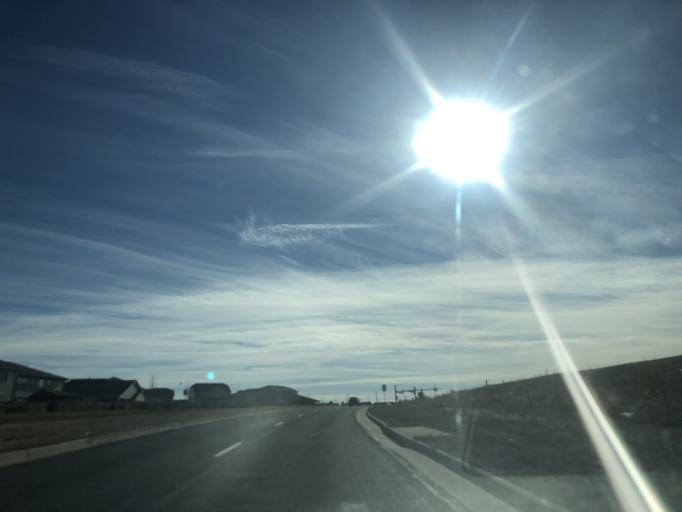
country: US
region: Colorado
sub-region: Douglas County
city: Stonegate
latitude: 39.5587
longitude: -104.8072
